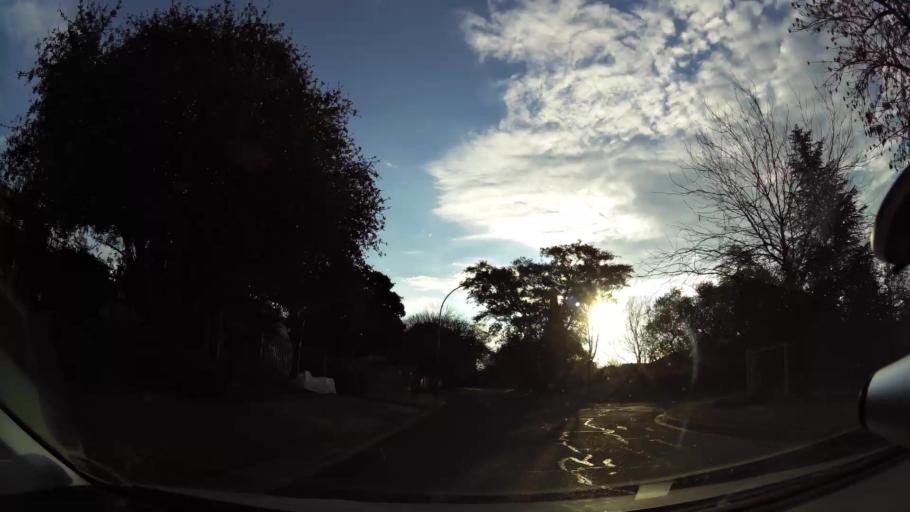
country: ZA
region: Orange Free State
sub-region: Mangaung Metropolitan Municipality
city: Bloemfontein
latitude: -29.1429
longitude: 26.1863
